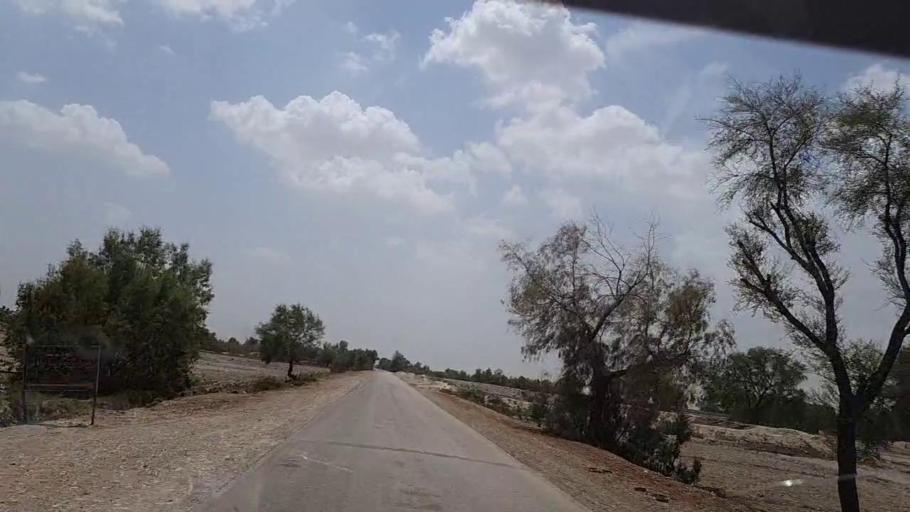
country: PK
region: Sindh
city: Bhan
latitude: 26.5409
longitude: 67.6627
